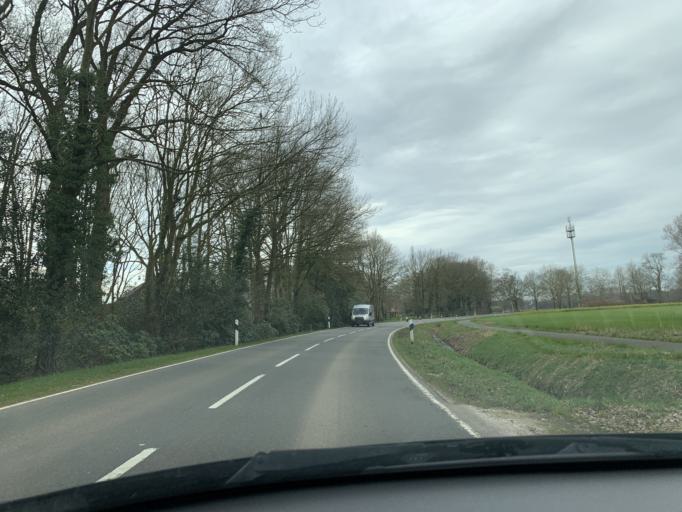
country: DE
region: Lower Saxony
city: Edewecht
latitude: 53.1501
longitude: 7.9658
